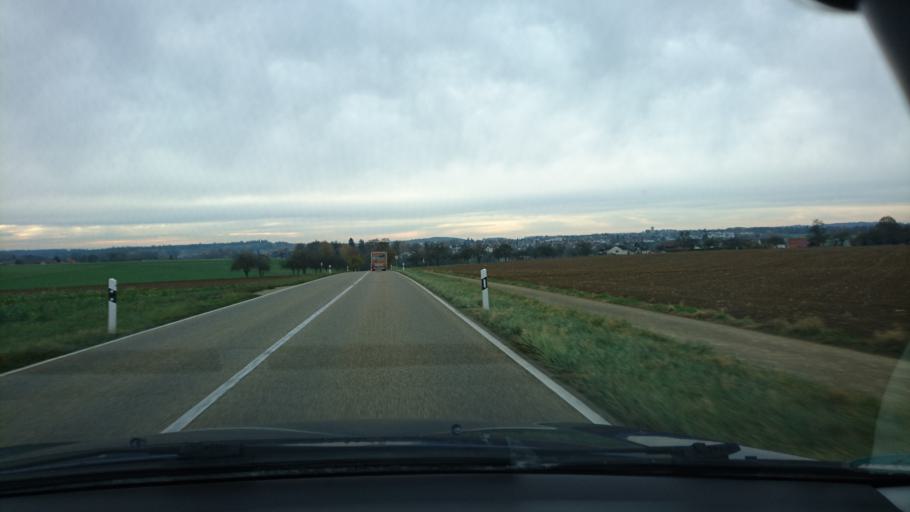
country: DE
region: Baden-Wuerttemberg
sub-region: Regierungsbezirk Stuttgart
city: Welzheim
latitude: 48.8883
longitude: 9.6502
